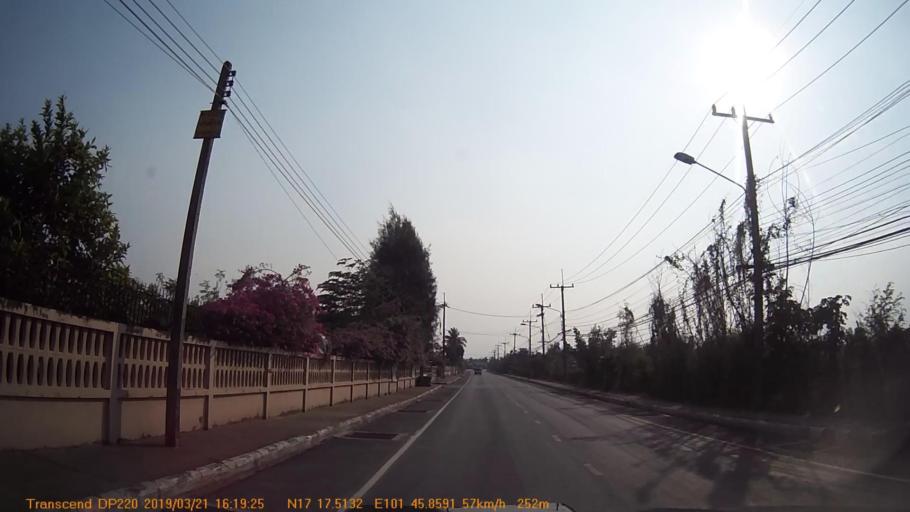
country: TH
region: Loei
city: Wang Saphung
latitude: 17.2918
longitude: 101.7642
